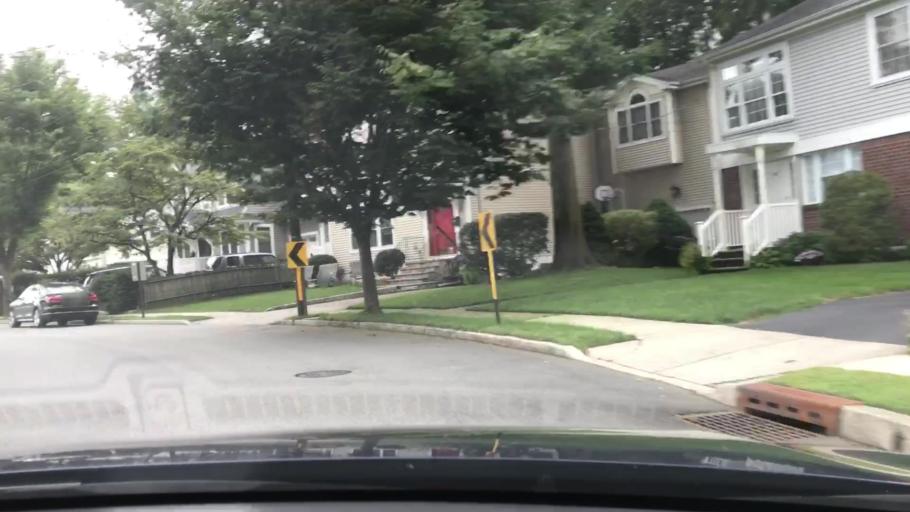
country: US
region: New Jersey
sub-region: Bergen County
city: New Milford
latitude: 40.9190
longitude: -74.0146
